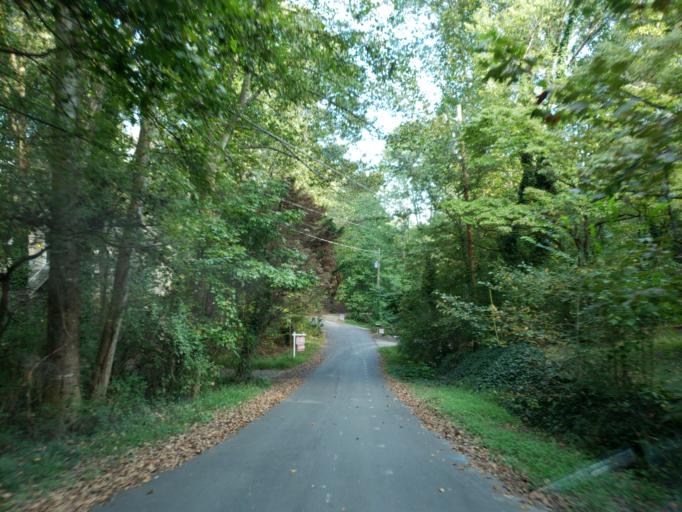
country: US
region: Georgia
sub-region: Fulton County
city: Roswell
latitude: 34.0794
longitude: -84.4078
